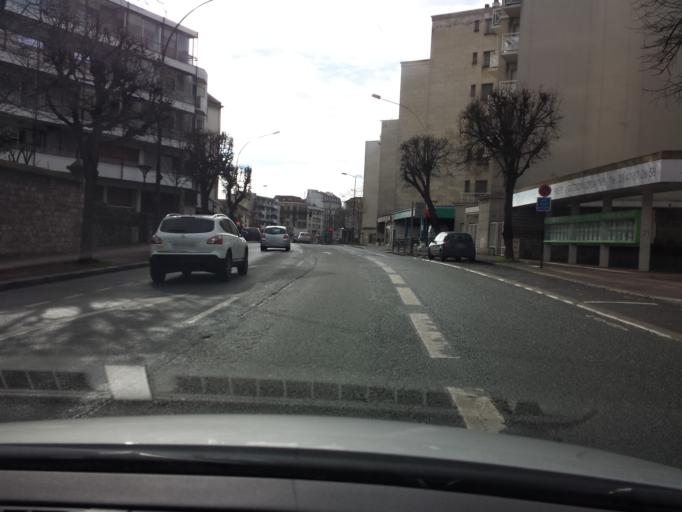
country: FR
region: Ile-de-France
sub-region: Departement des Hauts-de-Seine
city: Bourg-la-Reine
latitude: 48.7780
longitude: 2.3134
